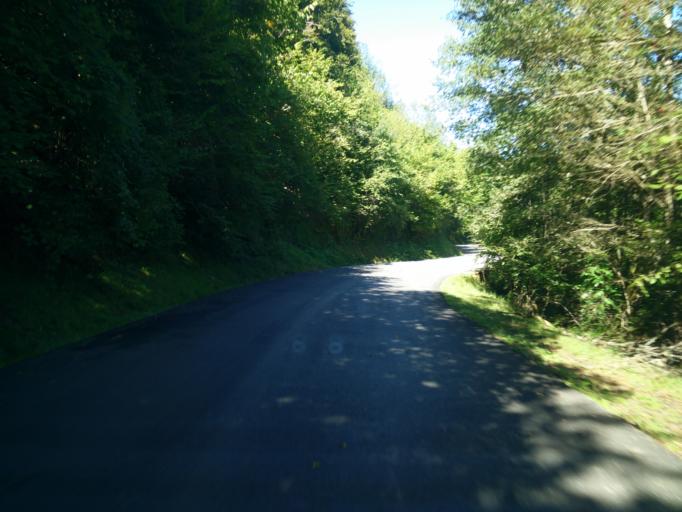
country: ES
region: Cantabria
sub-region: Provincia de Cantabria
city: Ruente
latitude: 43.1179
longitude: -4.2916
